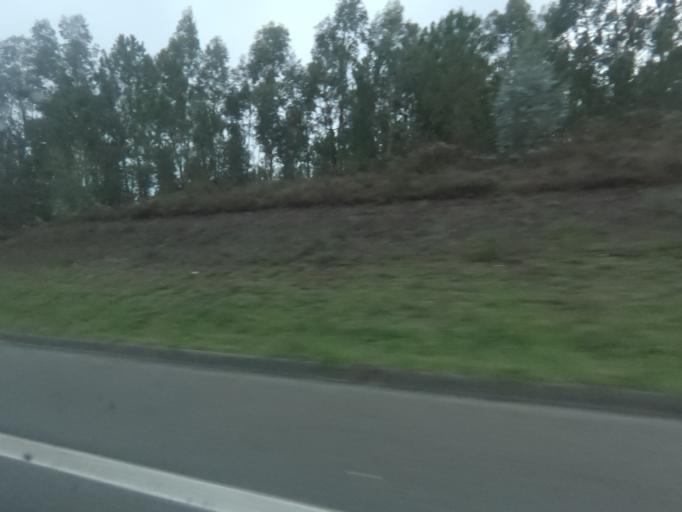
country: PT
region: Braga
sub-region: Vila Verde
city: Prado
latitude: 41.5428
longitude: -8.4979
